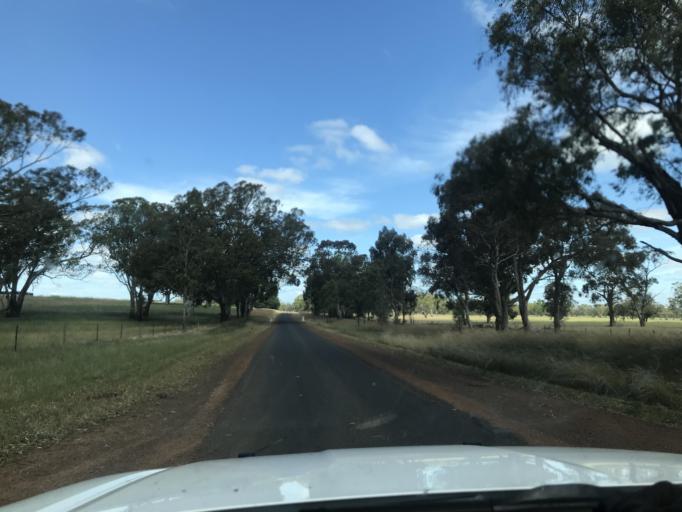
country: AU
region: South Australia
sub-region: Naracoorte and Lucindale
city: Naracoorte
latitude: -36.8638
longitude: 141.1705
